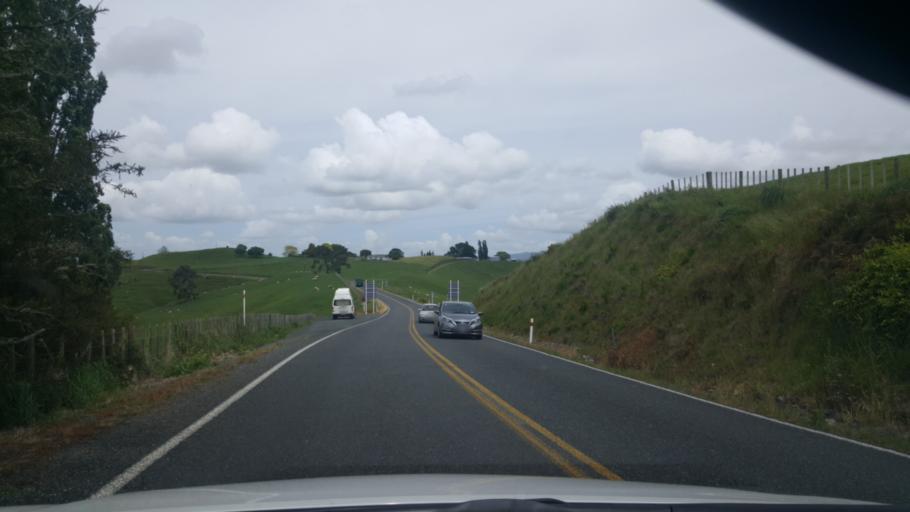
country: NZ
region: Waikato
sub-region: Matamata-Piako District
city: Matamata
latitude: -37.8723
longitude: 175.6862
